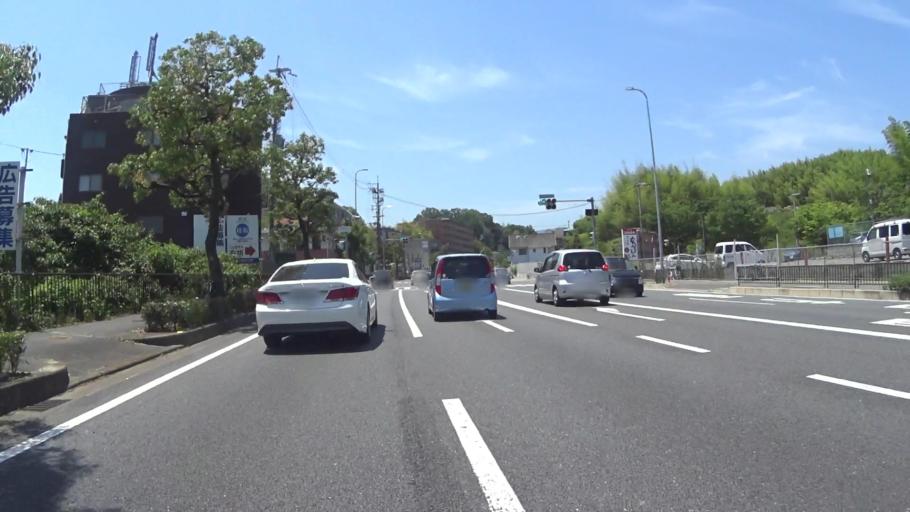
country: JP
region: Kyoto
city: Muko
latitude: 34.9768
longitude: 135.6887
